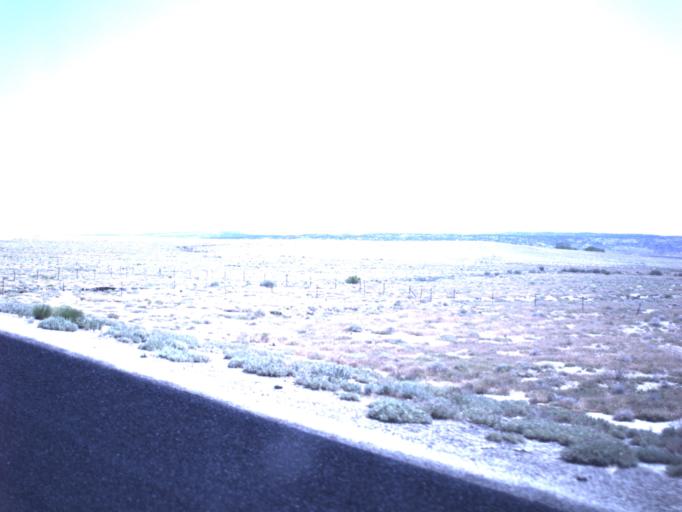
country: US
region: Utah
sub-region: Emery County
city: Ferron
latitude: 38.9684
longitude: -111.1860
